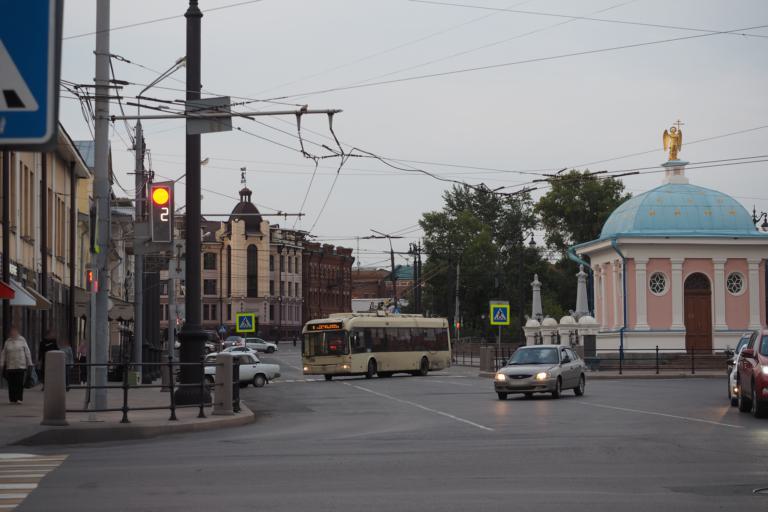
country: RU
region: Tomsk
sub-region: Tomskiy Rayon
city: Tomsk
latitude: 56.4885
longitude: 84.9477
